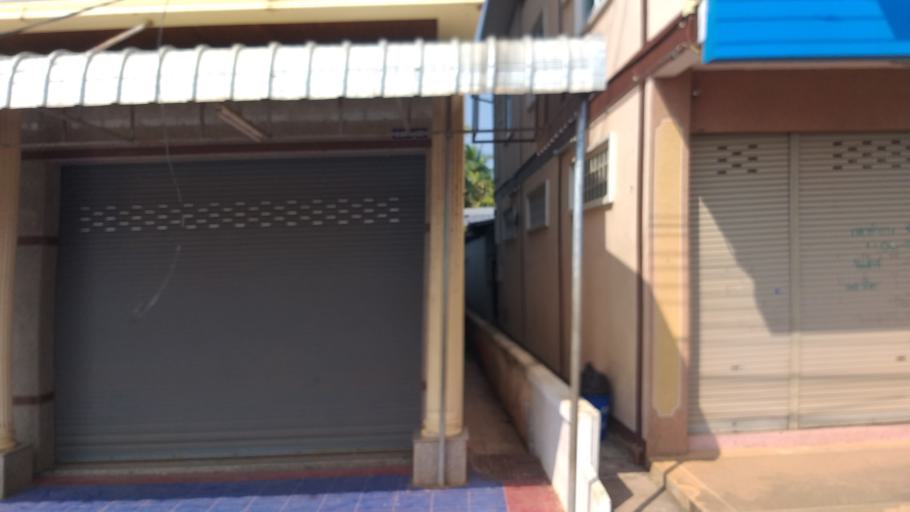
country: TH
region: Changwat Udon Thani
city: Nong Han
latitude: 17.3629
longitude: 103.1012
